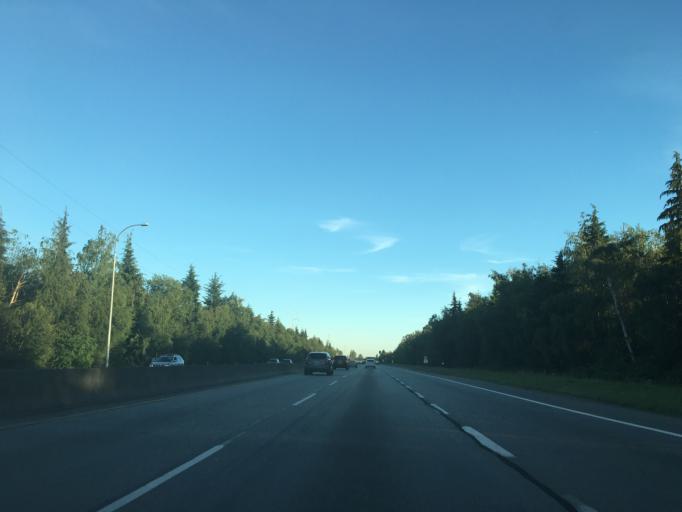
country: CA
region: British Columbia
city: Richmond
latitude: 49.1631
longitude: -123.0868
